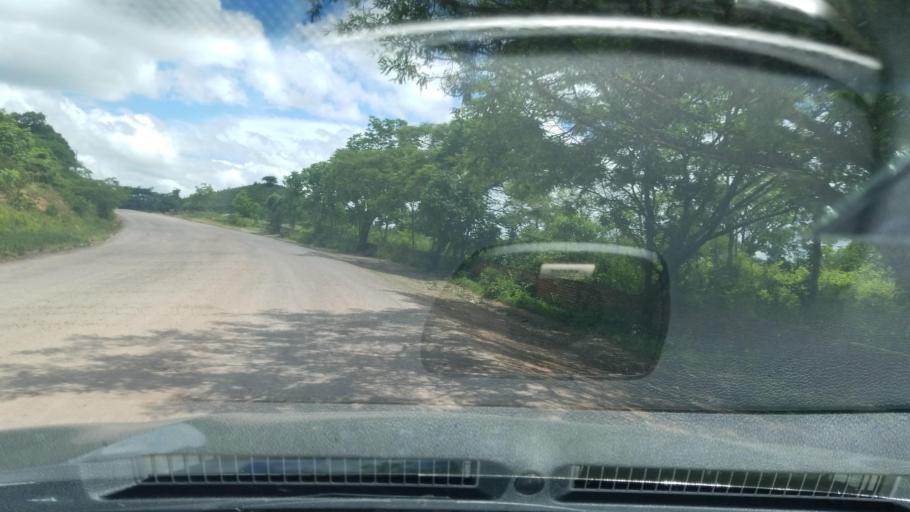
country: HN
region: Francisco Morazan
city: Talanga
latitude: 14.3562
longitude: -87.0451
